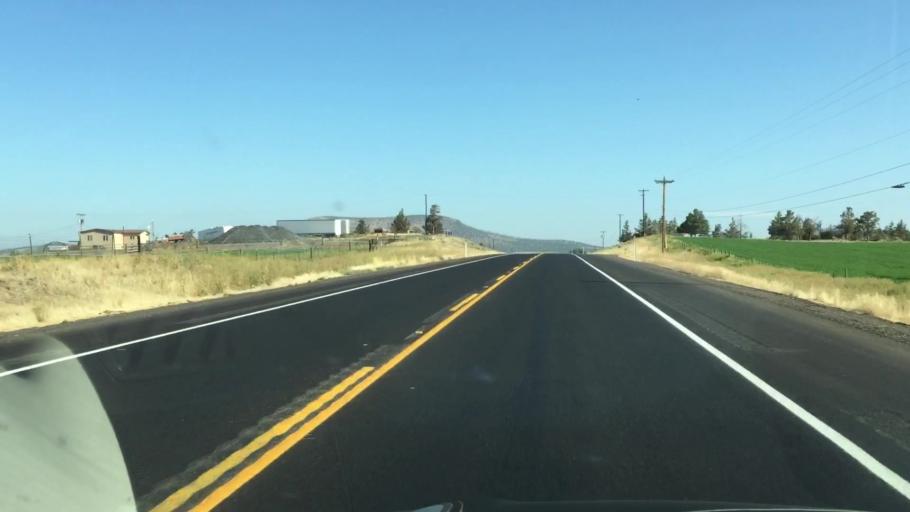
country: US
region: Oregon
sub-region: Deschutes County
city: Terrebonne
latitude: 44.4248
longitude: -121.1992
